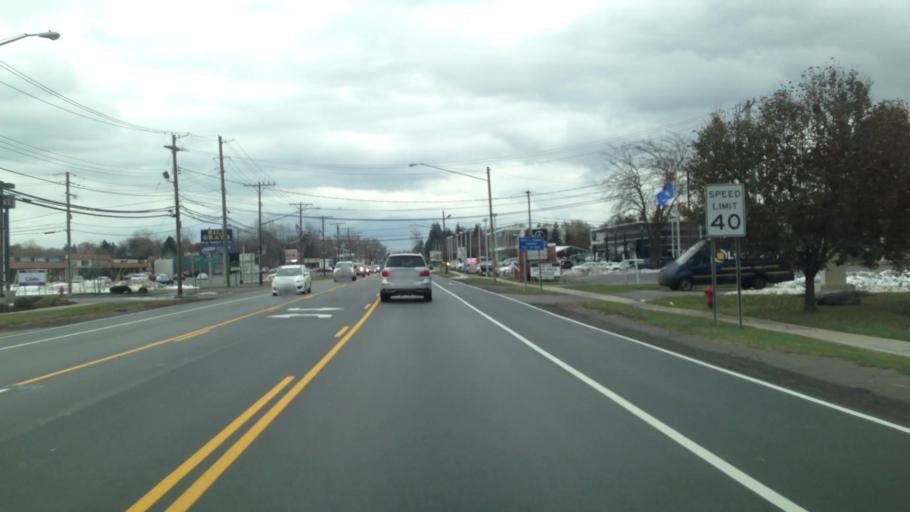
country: US
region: New York
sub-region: Erie County
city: Harris Hill
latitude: 42.9650
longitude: -78.6913
